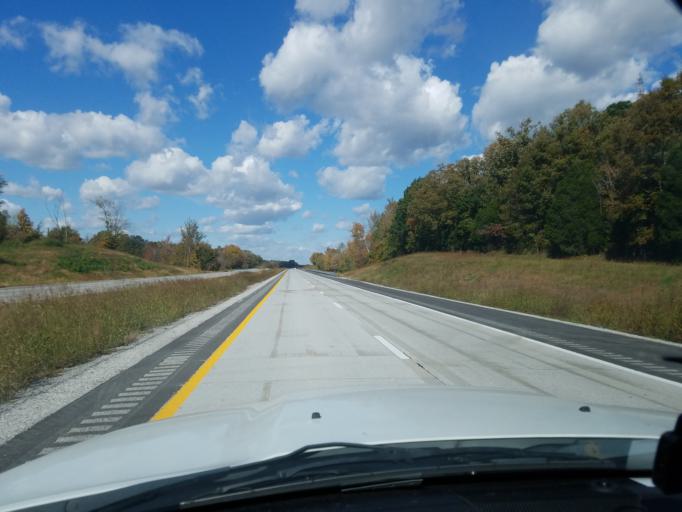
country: US
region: Kentucky
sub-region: Ohio County
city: Oak Grove
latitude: 37.3599
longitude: -86.7926
